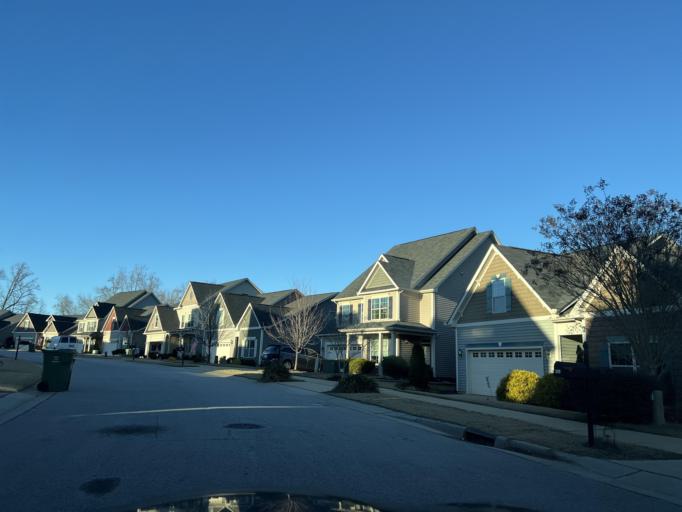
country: US
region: North Carolina
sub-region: Wake County
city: Fuquay-Varina
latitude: 35.5752
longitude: -78.8122
